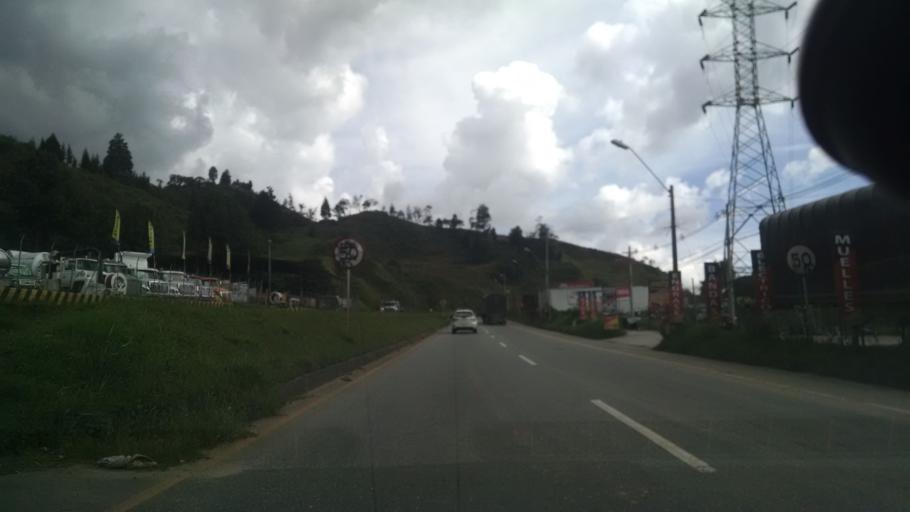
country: CO
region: Antioquia
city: Caldas
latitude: 6.0861
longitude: -75.6310
